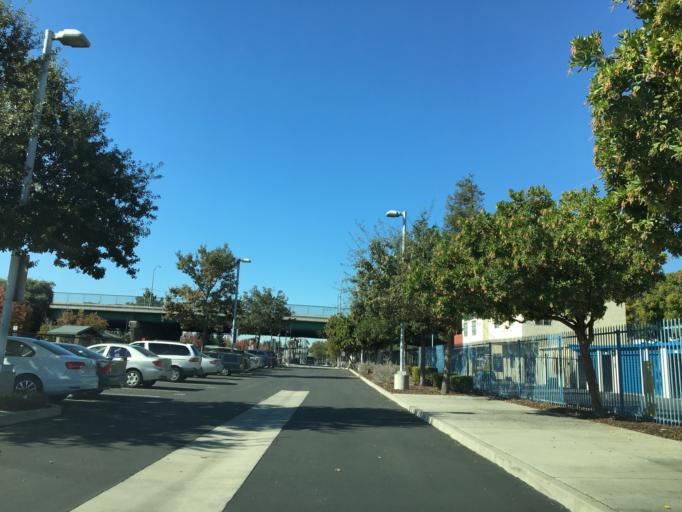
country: US
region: California
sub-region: Santa Clara County
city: Sunnyvale
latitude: 37.3707
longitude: -121.9949
